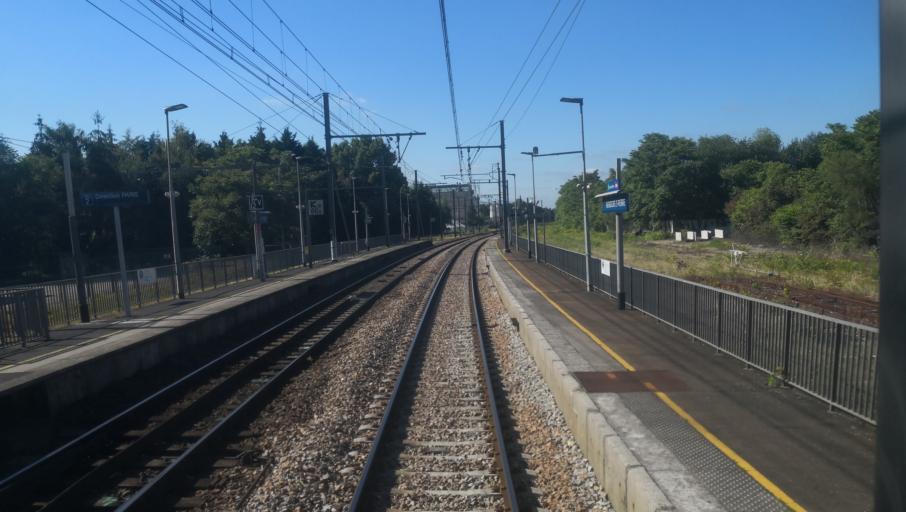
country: FR
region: Ile-de-France
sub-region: Departement de Seine-et-Marne
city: Saint-Pierre-les-Nemours
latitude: 48.2694
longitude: 2.6845
